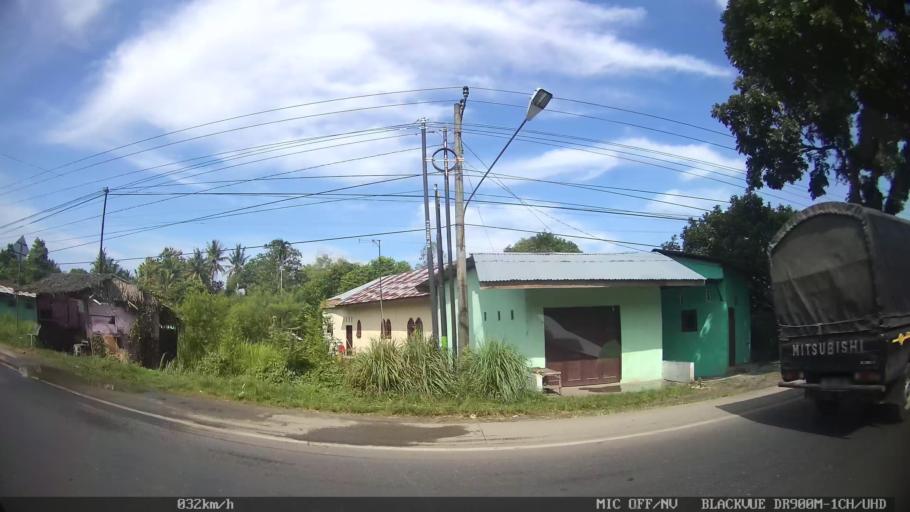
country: ID
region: North Sumatra
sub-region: Kabupaten Langkat
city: Stabat
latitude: 3.7102
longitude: 98.5052
